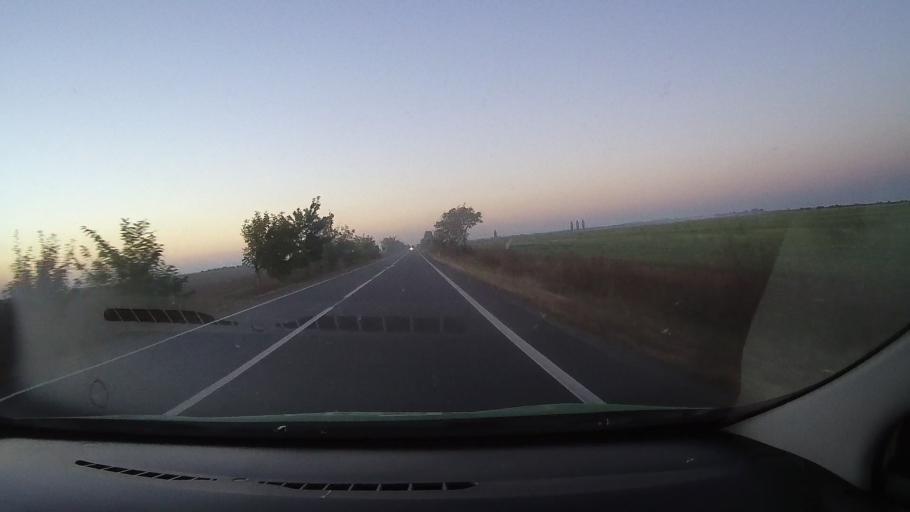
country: RO
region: Bihor
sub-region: Comuna Tarcea
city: Tarcea
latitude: 47.4811
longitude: 22.1624
